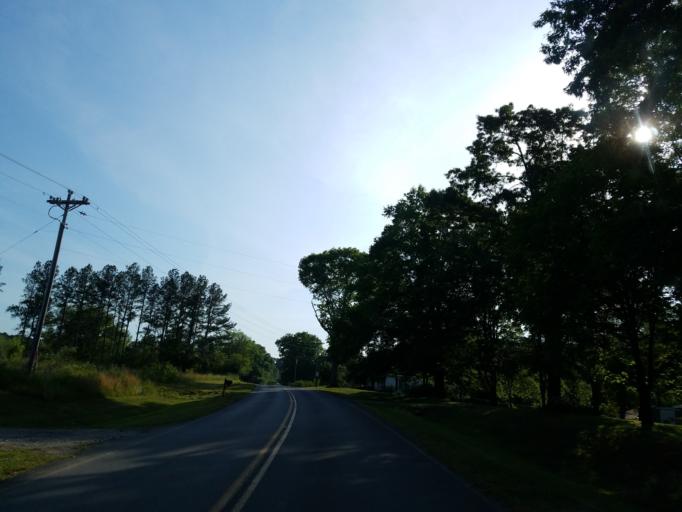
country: US
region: Georgia
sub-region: Chattooga County
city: Trion
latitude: 34.5626
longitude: -85.1831
